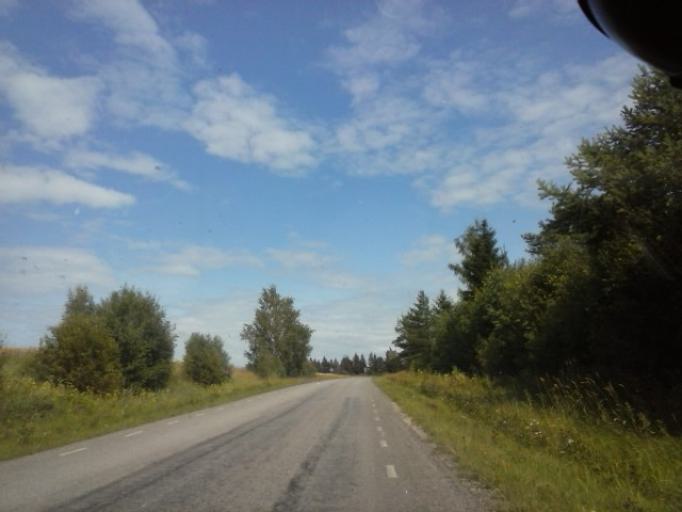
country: EE
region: Tartu
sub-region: UElenurme vald
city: Ulenurme
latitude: 58.2684
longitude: 26.9162
